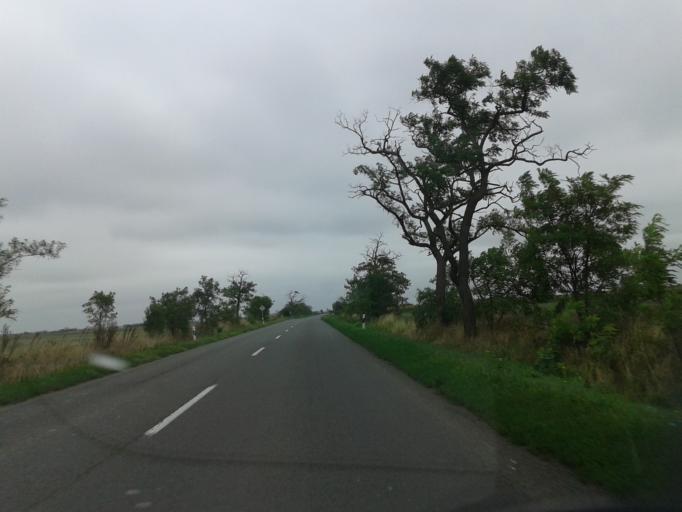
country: HU
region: Bacs-Kiskun
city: Harta
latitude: 46.7512
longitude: 19.1150
